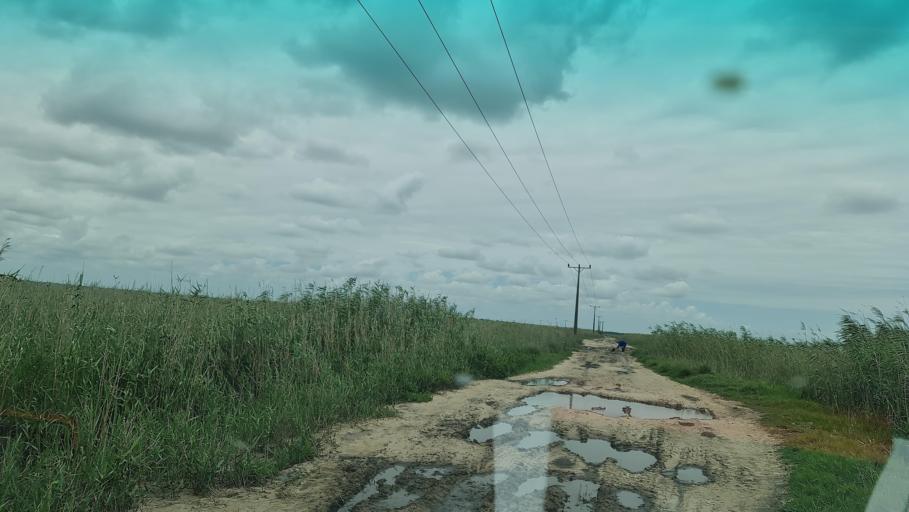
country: MZ
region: Maputo City
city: Maputo
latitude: -25.7190
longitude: 32.7004
